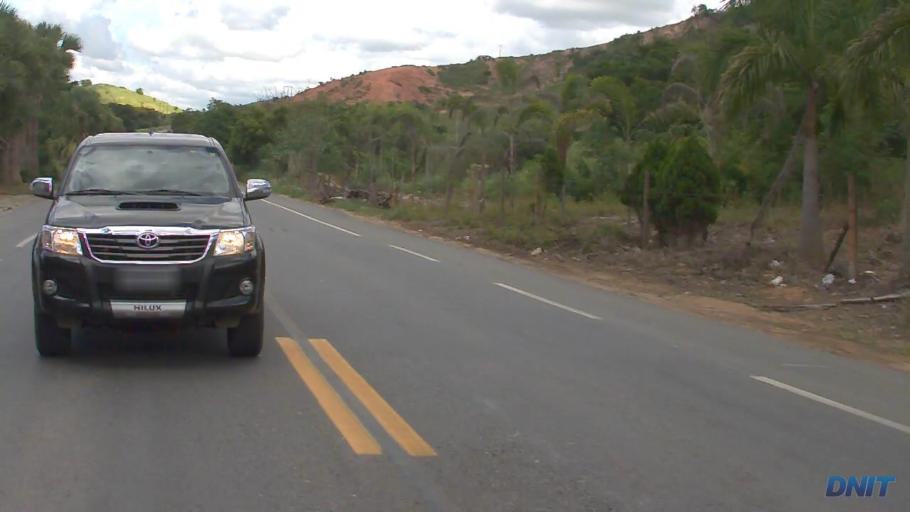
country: BR
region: Minas Gerais
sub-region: Governador Valadares
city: Governador Valadares
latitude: -18.9513
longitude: -42.0712
